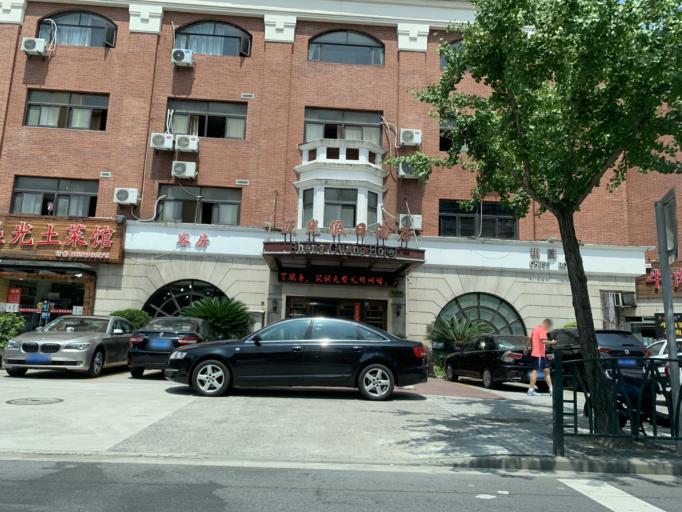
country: CN
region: Shanghai Shi
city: Huamu
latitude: 31.2048
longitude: 121.5137
